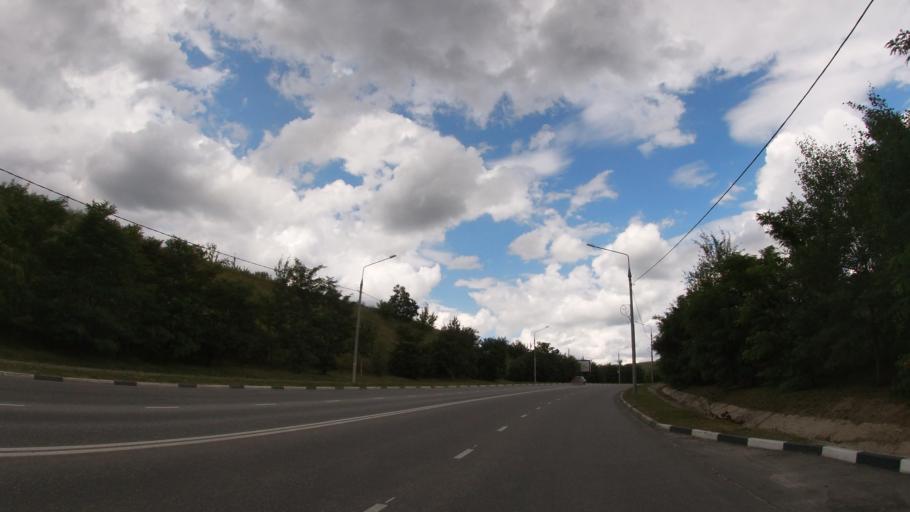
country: RU
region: Belgorod
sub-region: Belgorodskiy Rayon
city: Belgorod
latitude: 50.6105
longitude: 36.6127
